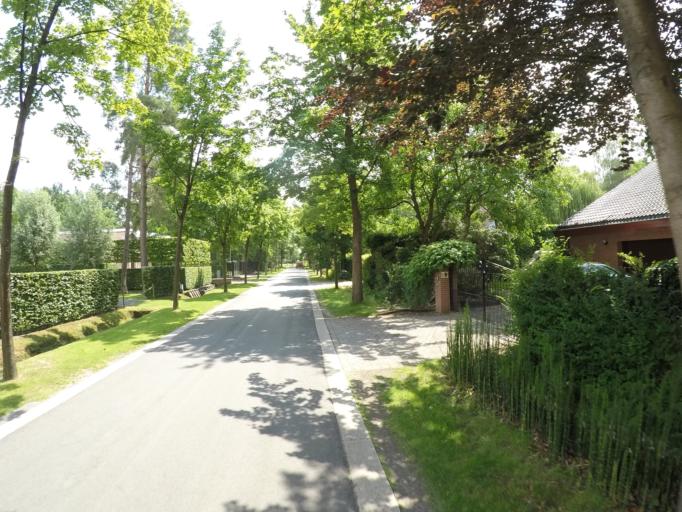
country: BE
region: Flanders
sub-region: Provincie Antwerpen
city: Schilde
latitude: 51.2573
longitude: 4.6015
